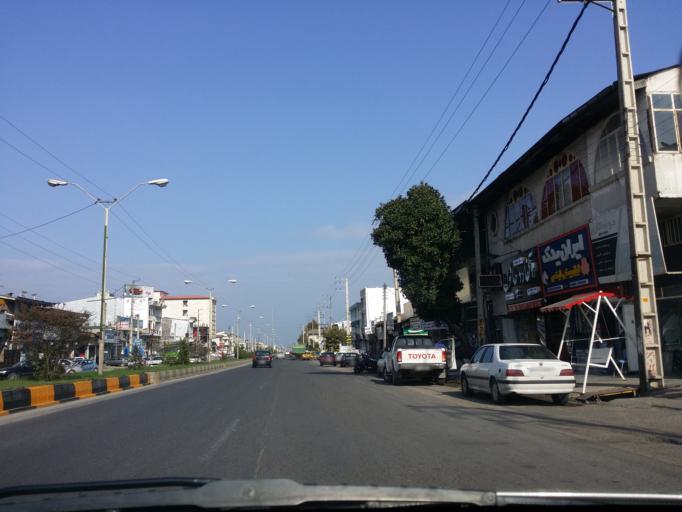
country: IR
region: Mazandaran
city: Chalus
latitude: 36.6675
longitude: 51.4095
